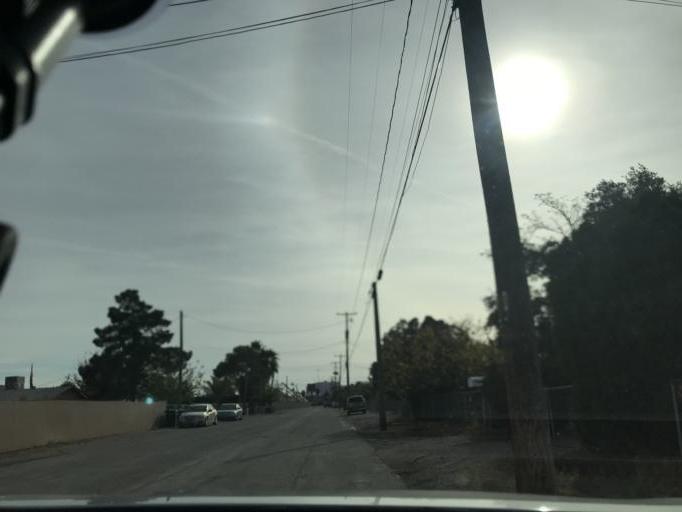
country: US
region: Nevada
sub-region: Clark County
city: Las Vegas
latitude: 36.1807
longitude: -115.1671
